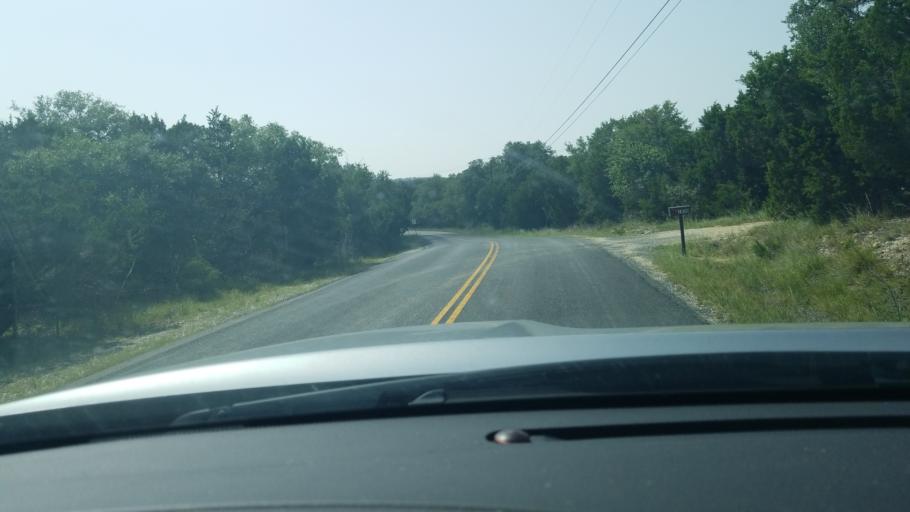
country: US
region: Texas
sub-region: Comal County
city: Bulverde
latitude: 29.7963
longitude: -98.4432
